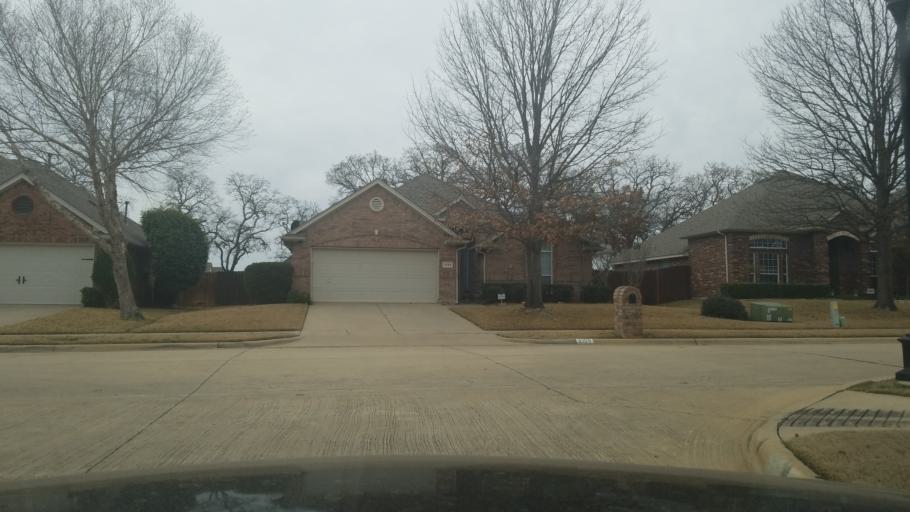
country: US
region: Texas
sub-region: Denton County
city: Corinth
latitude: 33.1336
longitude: -97.0758
